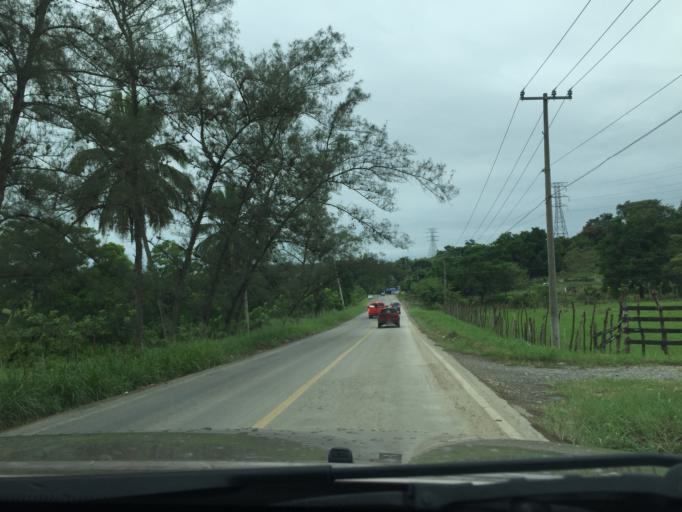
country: MX
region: Veracruz
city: Coatzintla
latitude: 20.4455
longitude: -97.4071
